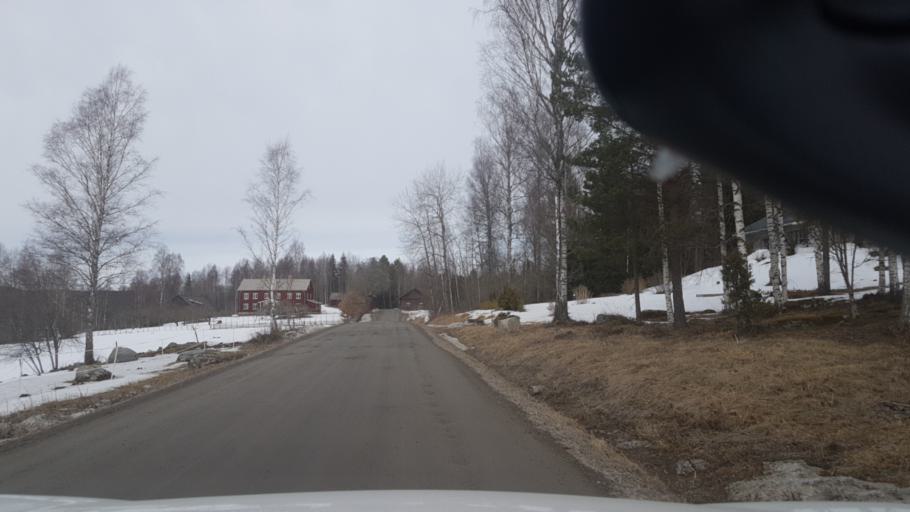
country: SE
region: Vaermland
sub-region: Eda Kommun
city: Amotfors
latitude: 59.7686
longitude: 12.4441
